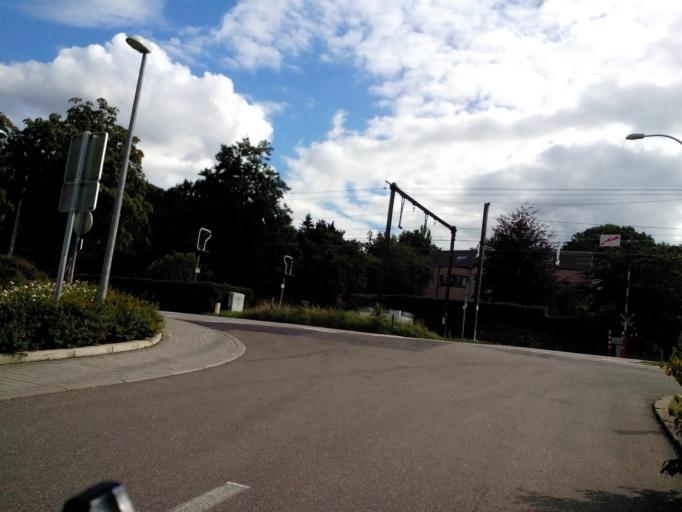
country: BE
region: Flanders
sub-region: Provincie Vlaams-Brabant
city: Oud-Heverlee
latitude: 50.8579
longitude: 4.6795
